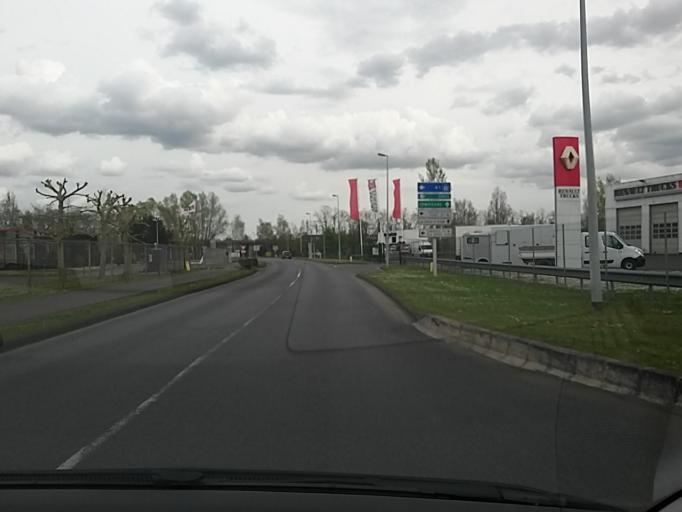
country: FR
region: Picardie
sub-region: Departement de l'Oise
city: Le Meux
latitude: 49.3579
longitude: 2.7553
